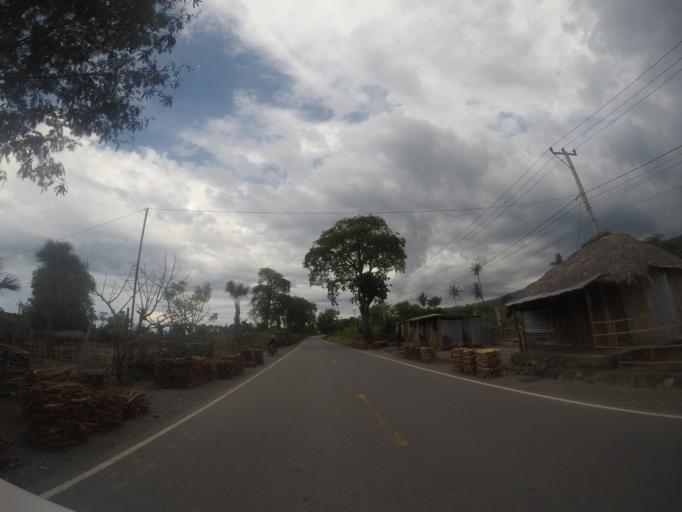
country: TL
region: Liquica
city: Liquica
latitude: -8.6045
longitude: 125.2950
